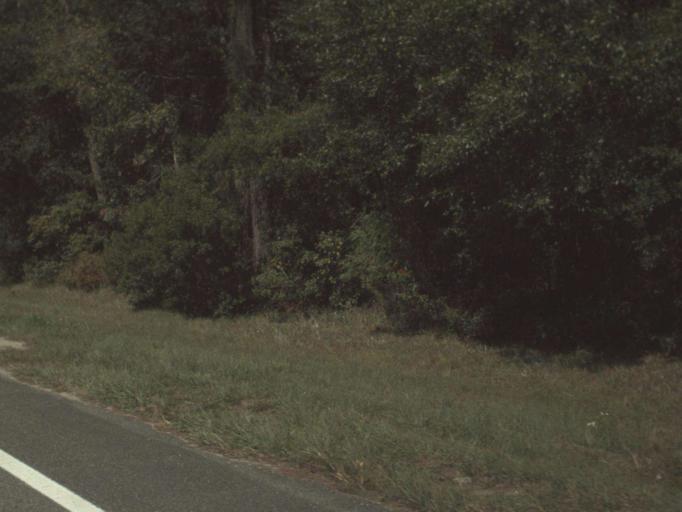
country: US
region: Florida
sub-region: Jefferson County
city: Monticello
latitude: 30.5019
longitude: -83.7560
